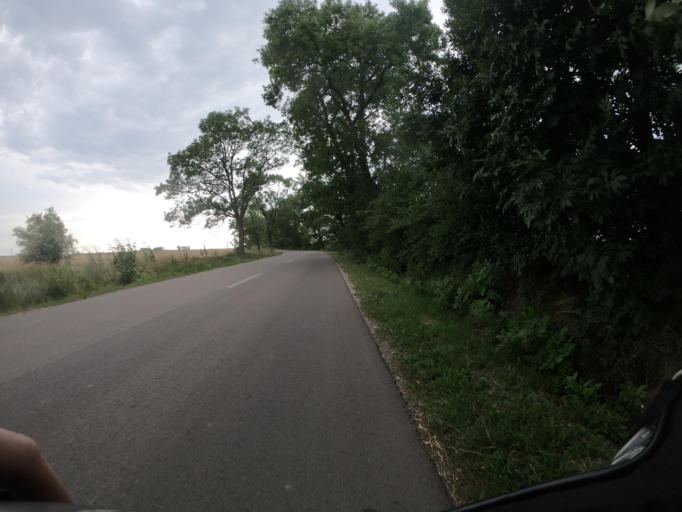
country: HU
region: Borsod-Abauj-Zemplen
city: Mezocsat
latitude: 47.8188
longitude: 20.8681
